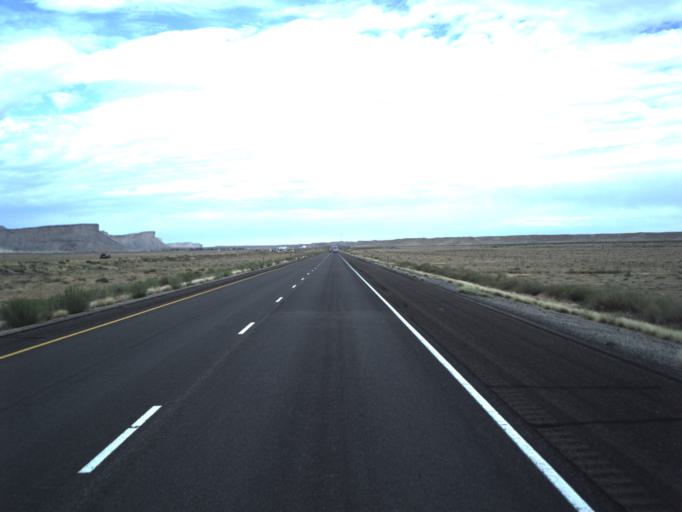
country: US
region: Utah
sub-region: Grand County
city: Moab
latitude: 38.9497
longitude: -109.7765
